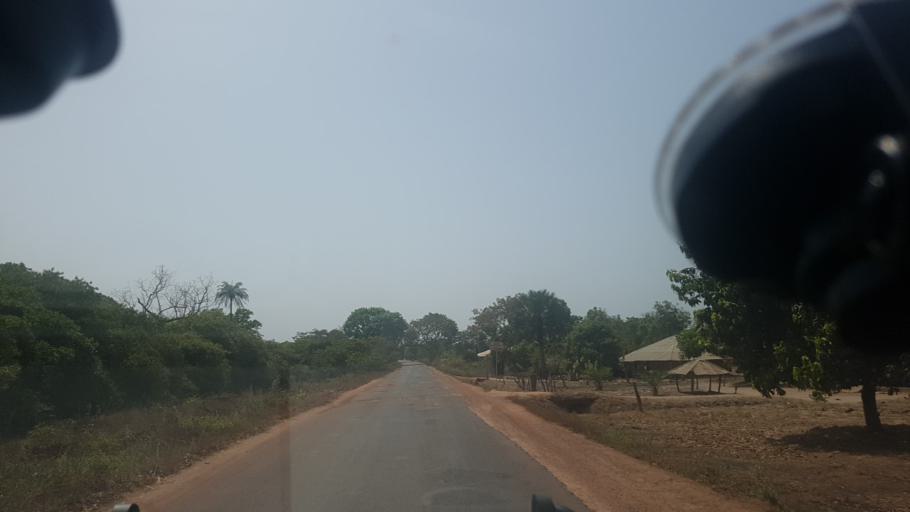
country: GW
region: Cacheu
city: Cacheu
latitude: 12.4096
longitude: -16.0420
